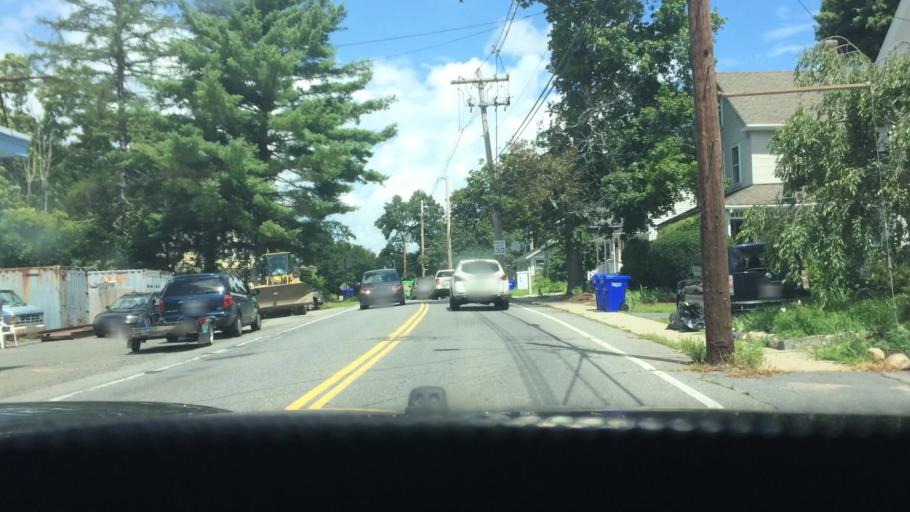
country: US
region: Massachusetts
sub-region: Middlesex County
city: Maynard
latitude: 42.4380
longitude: -71.4523
